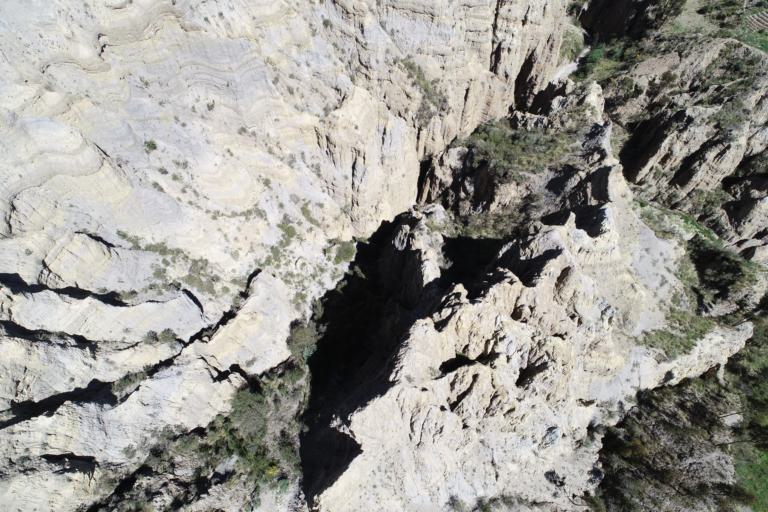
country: BO
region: La Paz
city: La Paz
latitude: -16.5029
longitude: -68.0635
